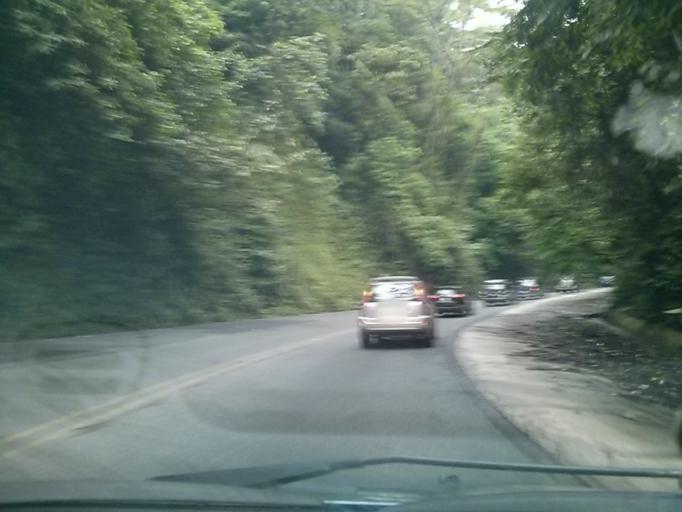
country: CR
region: San Jose
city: Dulce Nombre de Jesus
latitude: 10.1458
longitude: -83.9554
